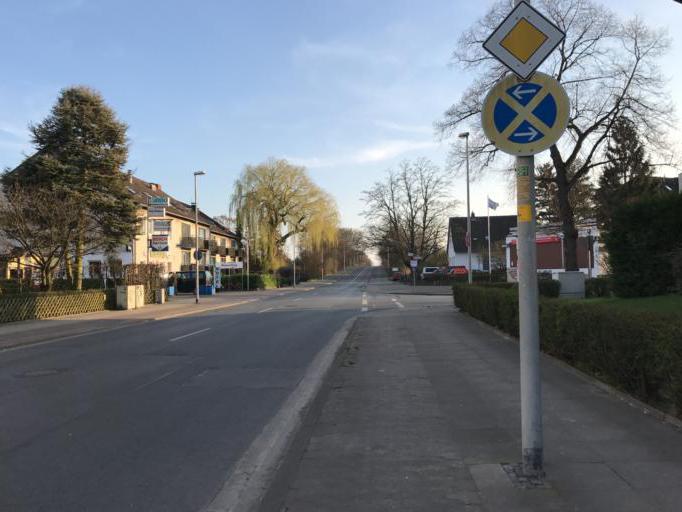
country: DE
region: Lower Saxony
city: Laatzen
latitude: 52.3471
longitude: 9.7812
